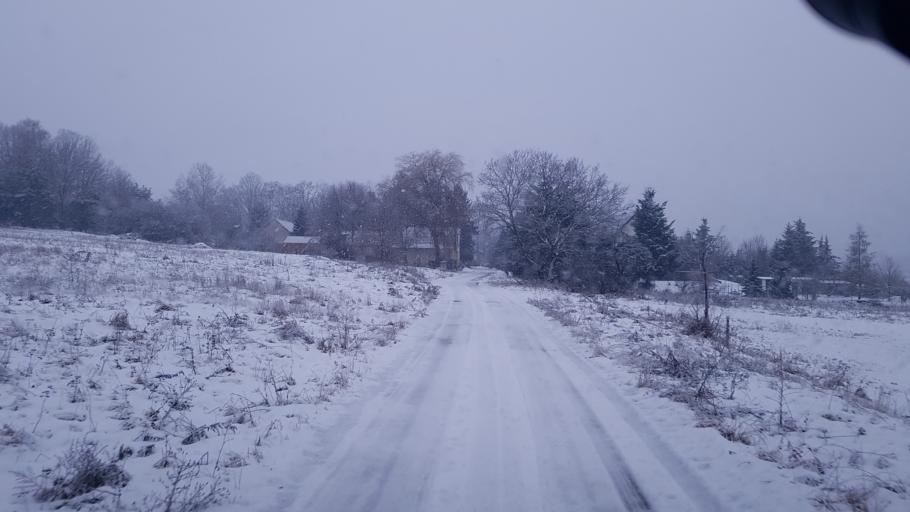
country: DE
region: Brandenburg
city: Schenkendobern
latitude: 51.9058
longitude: 14.5824
